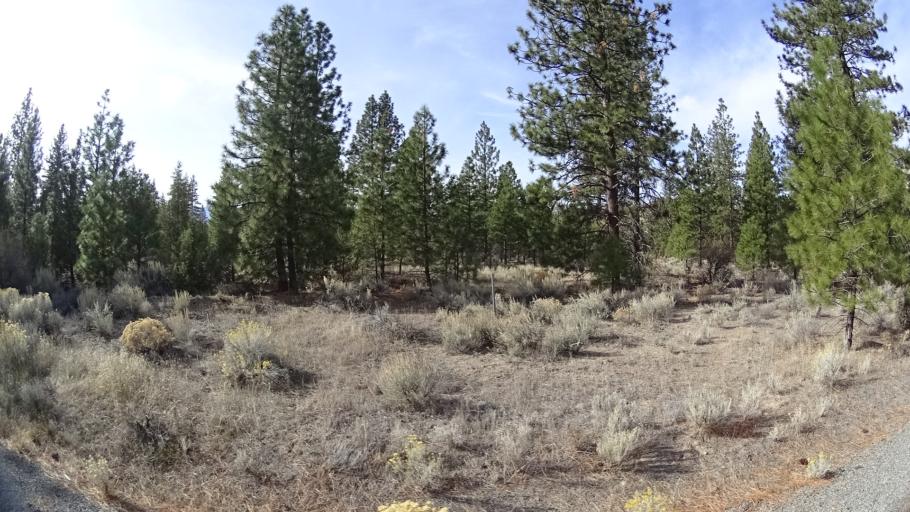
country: US
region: California
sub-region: Siskiyou County
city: Weed
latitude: 41.4975
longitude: -122.3809
